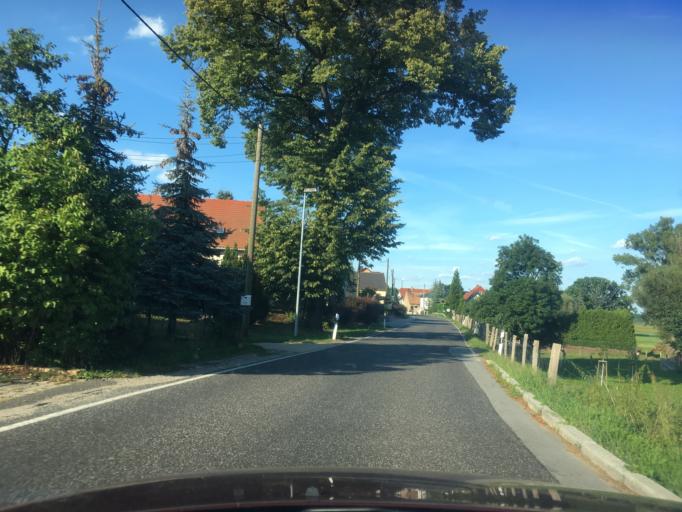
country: PL
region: Lower Silesian Voivodeship
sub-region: Powiat zgorzelecki
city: Piensk
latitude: 51.2158
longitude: 15.0021
